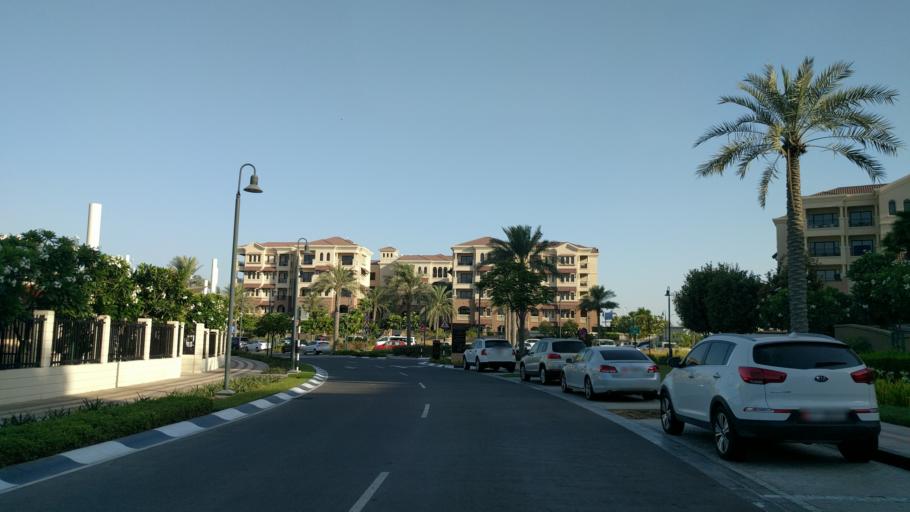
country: AE
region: Abu Dhabi
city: Abu Dhabi
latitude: 24.5510
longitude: 54.4524
